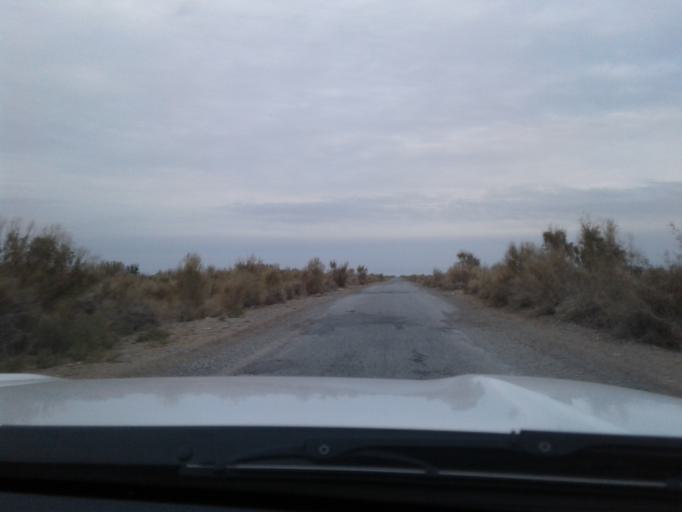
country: TM
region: Mary
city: Mary
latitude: 38.0548
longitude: 61.8354
